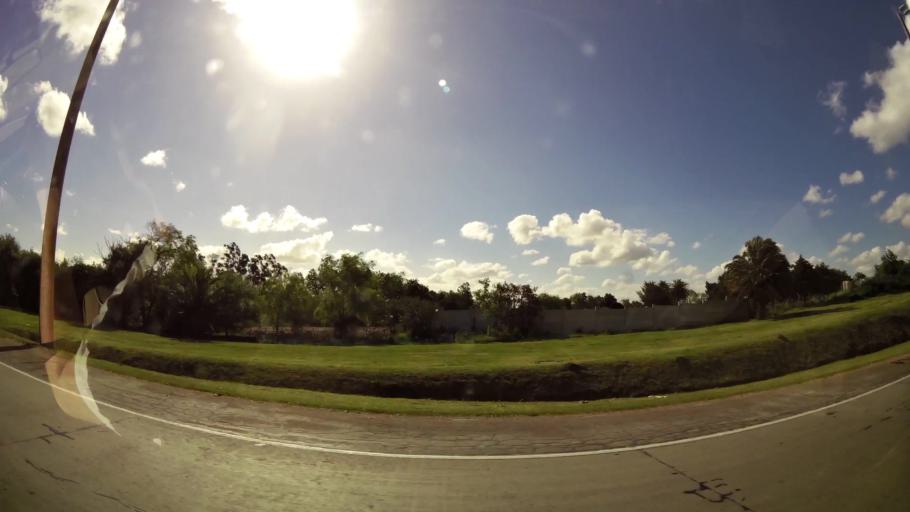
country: UY
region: Canelones
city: La Paz
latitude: -34.8290
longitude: -56.2517
